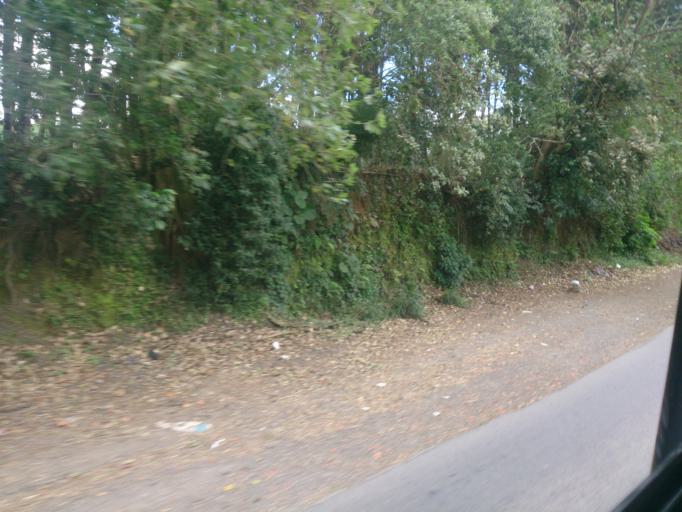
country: CR
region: San Jose
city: Granadilla
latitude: 9.9283
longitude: -84.0118
